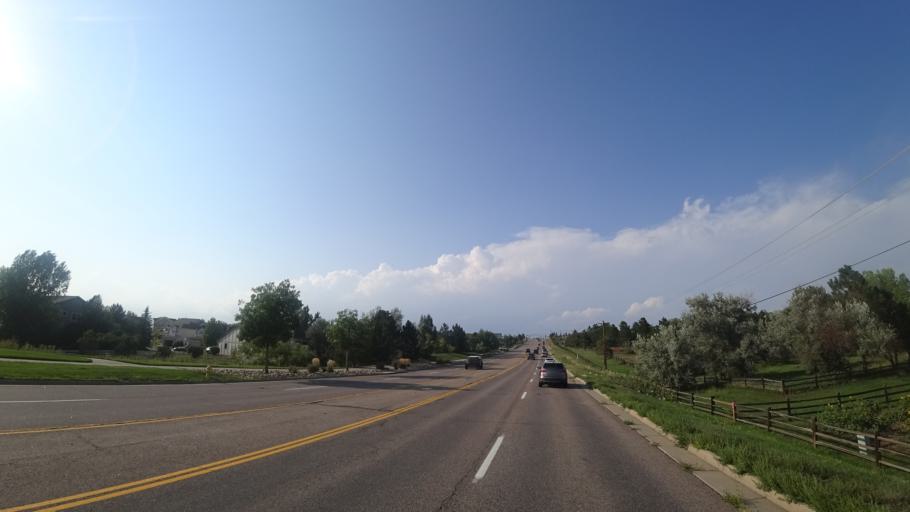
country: US
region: Colorado
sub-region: Douglas County
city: Parker
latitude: 39.6018
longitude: -104.7447
